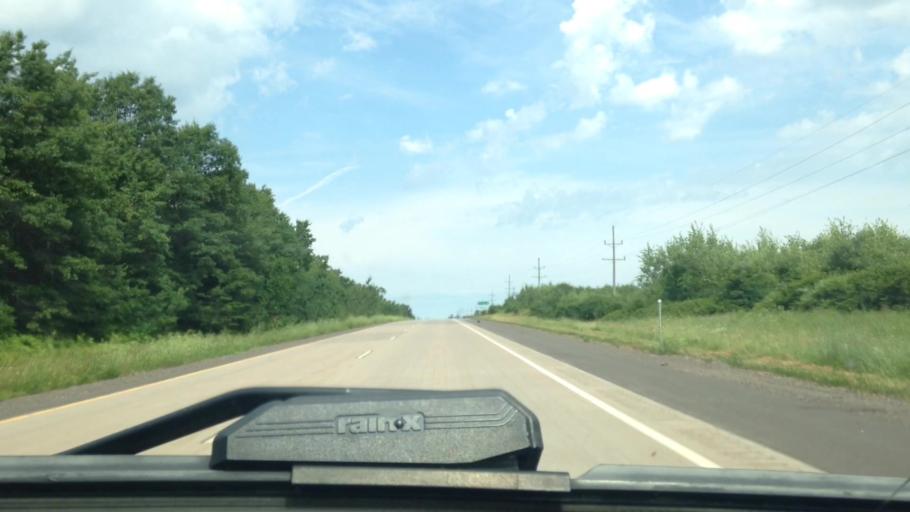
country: US
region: Wisconsin
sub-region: Douglas County
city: Lake Nebagamon
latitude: 46.2748
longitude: -91.8059
